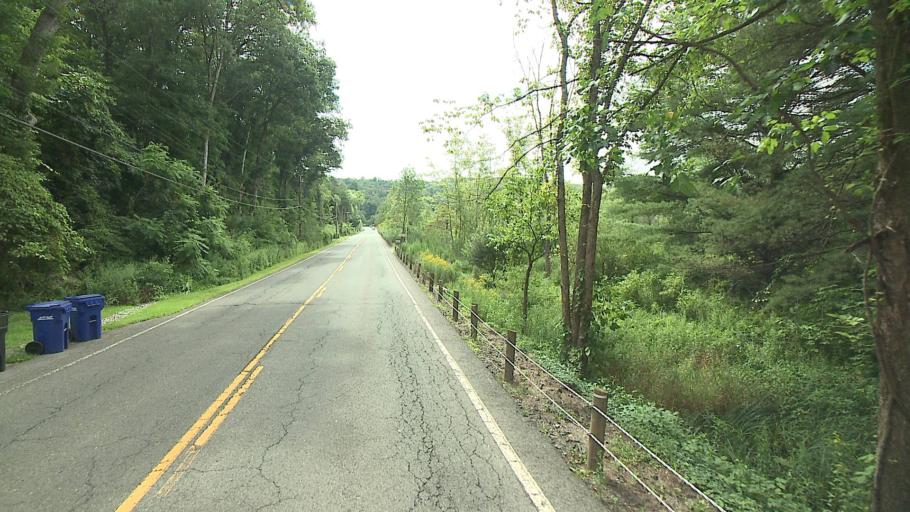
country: US
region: Connecticut
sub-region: Fairfield County
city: Sherman
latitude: 41.6416
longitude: -73.5012
